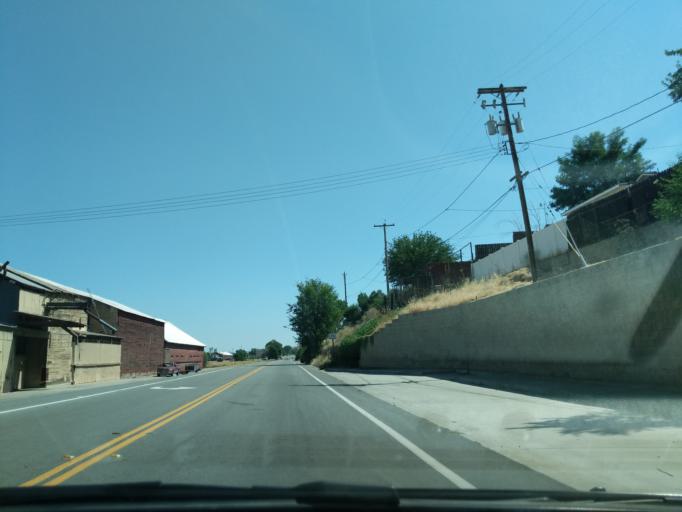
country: US
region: California
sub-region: San Luis Obispo County
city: San Miguel
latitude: 35.7592
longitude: -120.6953
